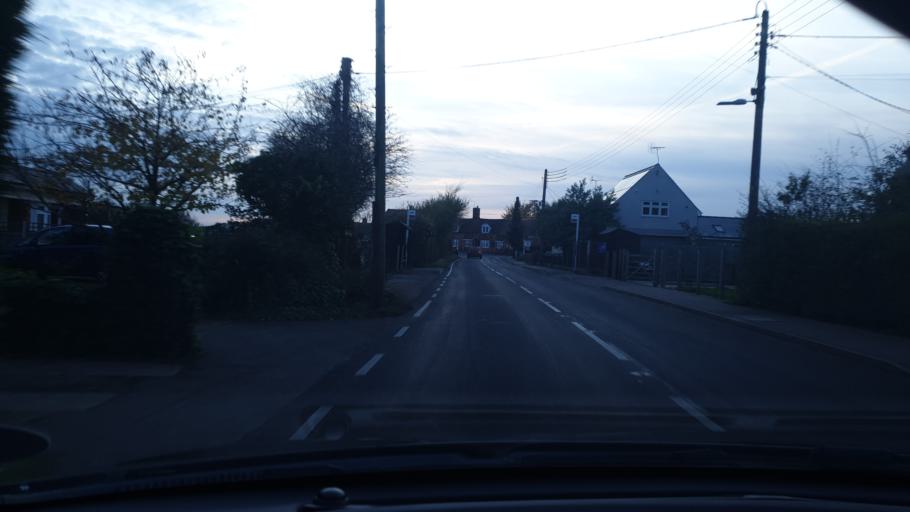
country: GB
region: England
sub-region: Essex
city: Dovercourt
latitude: 51.9165
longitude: 1.2242
